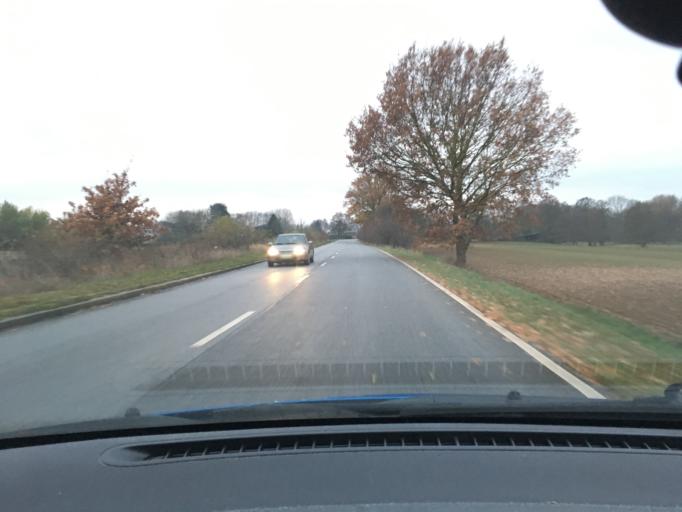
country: DE
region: Lower Saxony
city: Drage
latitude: 53.4217
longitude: 10.2085
